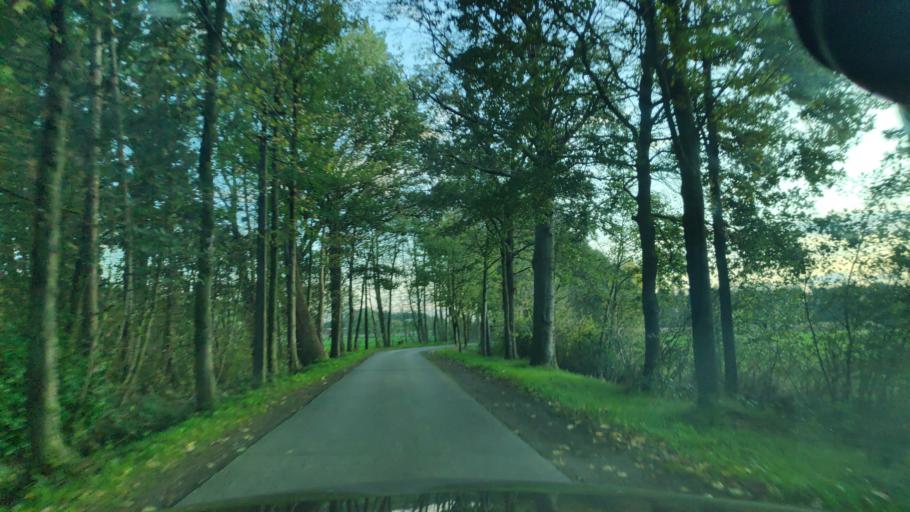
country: BE
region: Flanders
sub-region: Provincie Oost-Vlaanderen
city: Zomergem
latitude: 51.1364
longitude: 3.5074
